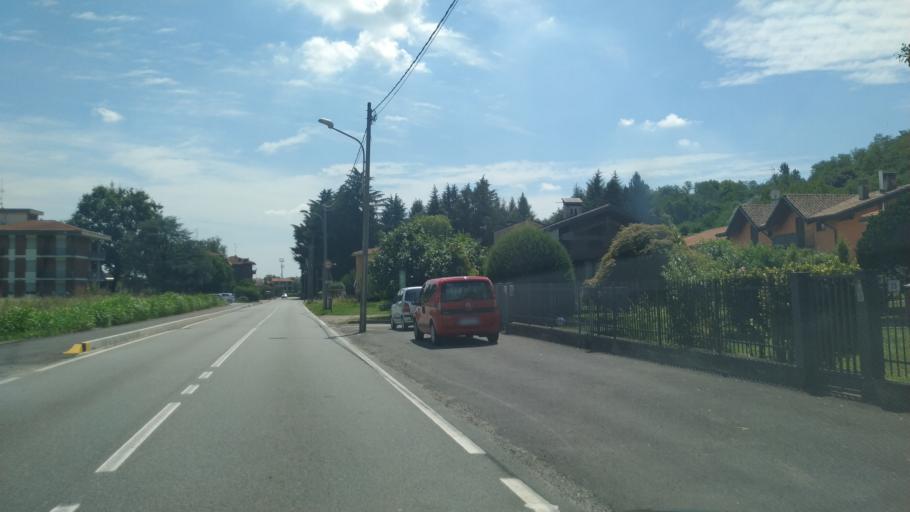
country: IT
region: Piedmont
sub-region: Provincia di Novara
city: Borgomanero
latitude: 45.6976
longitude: 8.4505
